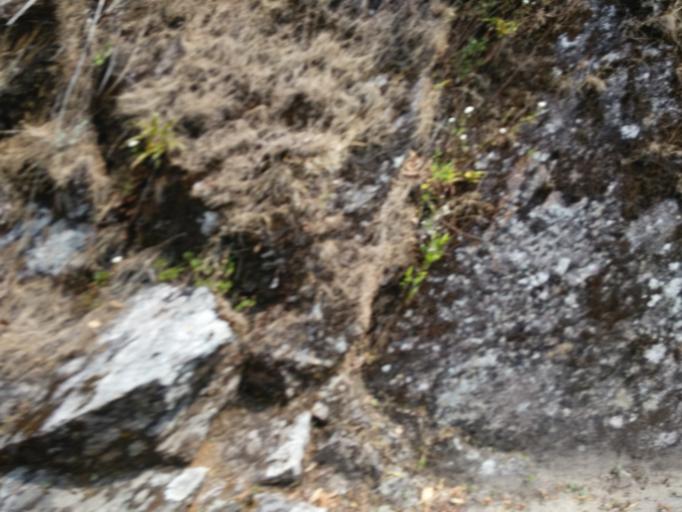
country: NP
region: Central Region
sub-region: Narayani Zone
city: Hitura
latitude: 27.5723
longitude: 85.0759
